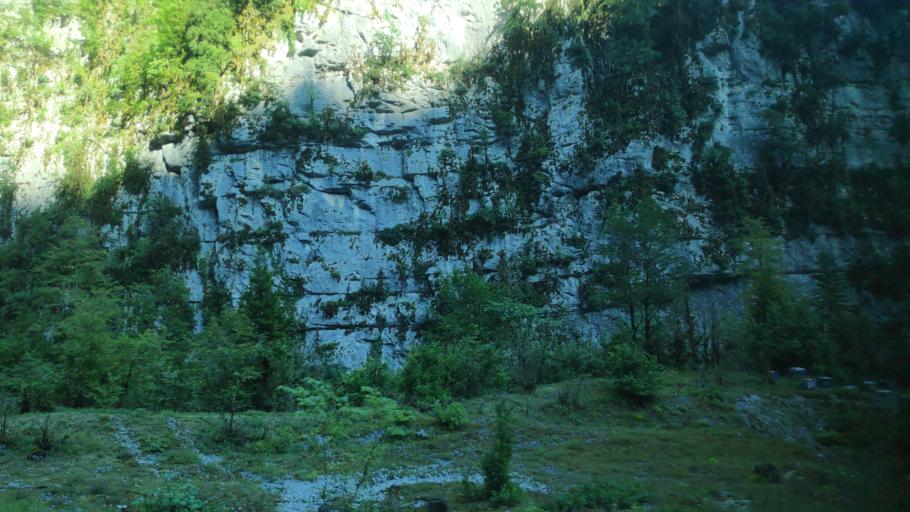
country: GE
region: Abkhazia
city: Gagra
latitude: 43.4347
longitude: 40.5306
